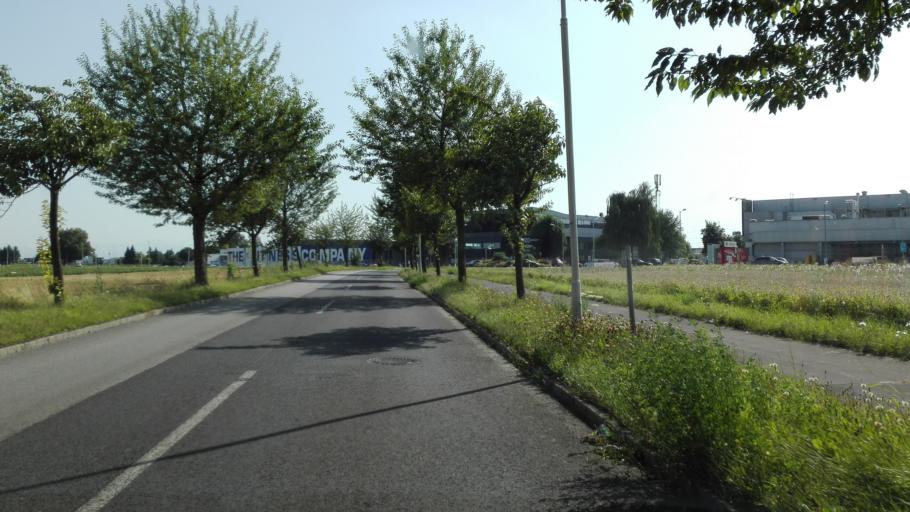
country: AT
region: Upper Austria
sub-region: Politischer Bezirk Linz-Land
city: Leonding
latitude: 48.2613
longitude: 14.2606
